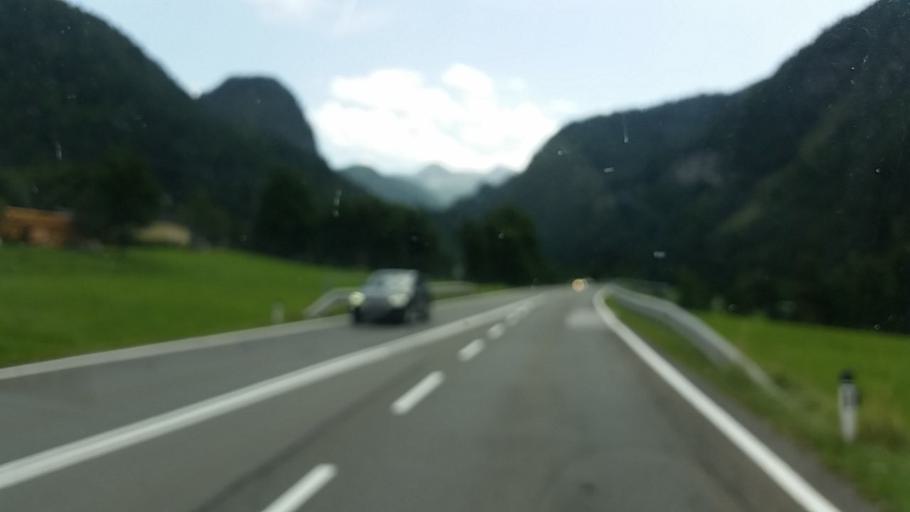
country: AT
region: Salzburg
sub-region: Politischer Bezirk Sankt Johann im Pongau
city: Untertauern
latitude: 47.3070
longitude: 13.5066
